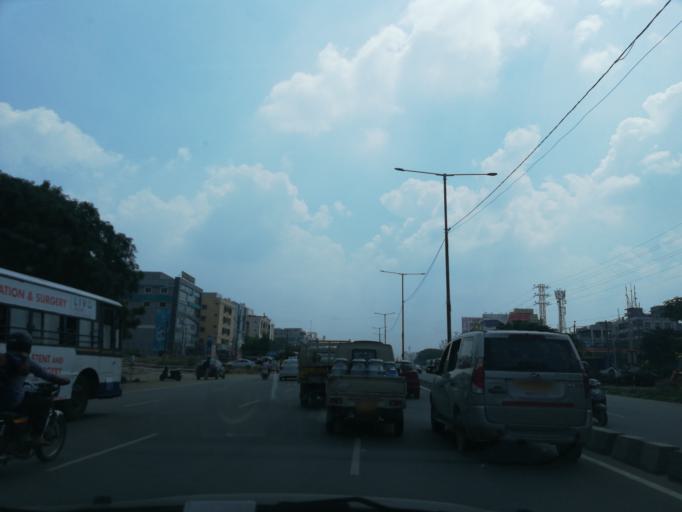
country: IN
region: Telangana
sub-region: Medak
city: Serilingampalle
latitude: 17.4956
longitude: 78.3354
